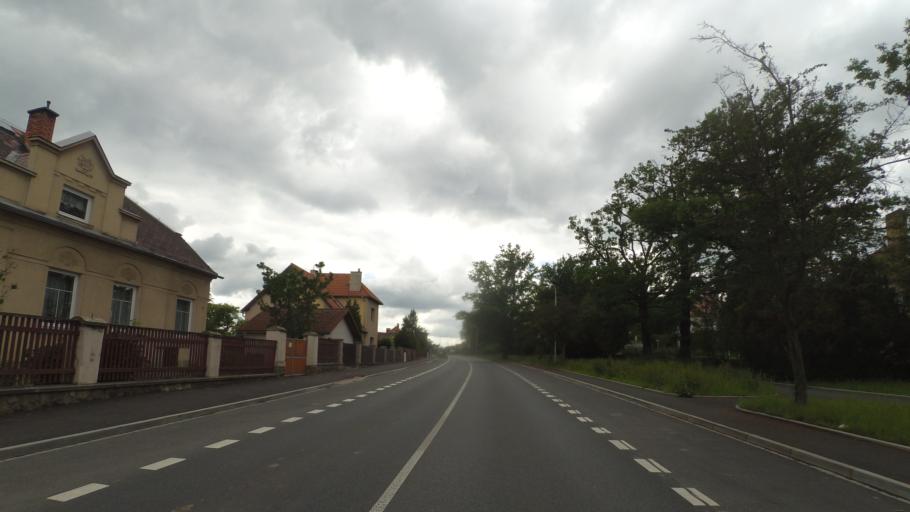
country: CZ
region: Plzensky
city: Horsovsky Tyn
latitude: 49.5311
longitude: 12.9363
